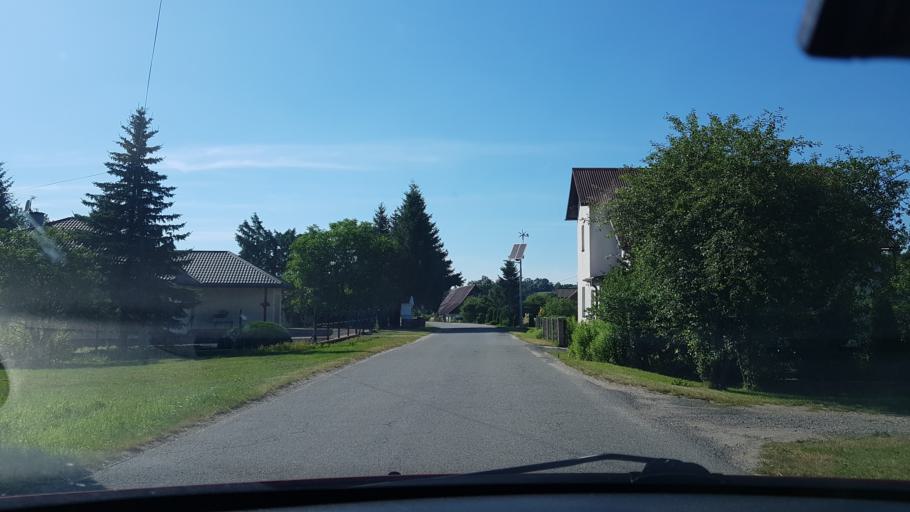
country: PL
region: Lower Silesian Voivodeship
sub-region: Powiat klodzki
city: Bystrzyca Klodzka
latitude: 50.2440
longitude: 16.7090
